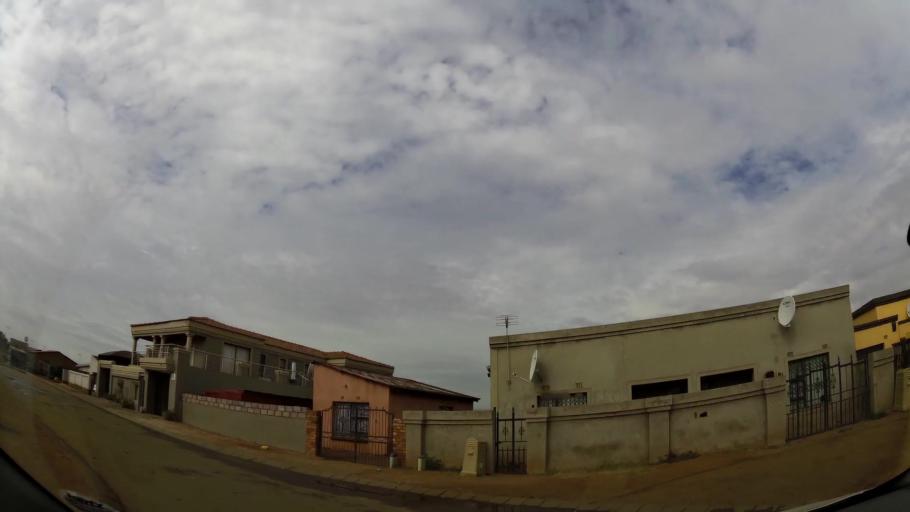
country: ZA
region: Gauteng
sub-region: Ekurhuleni Metropolitan Municipality
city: Germiston
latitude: -26.3804
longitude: 28.1638
